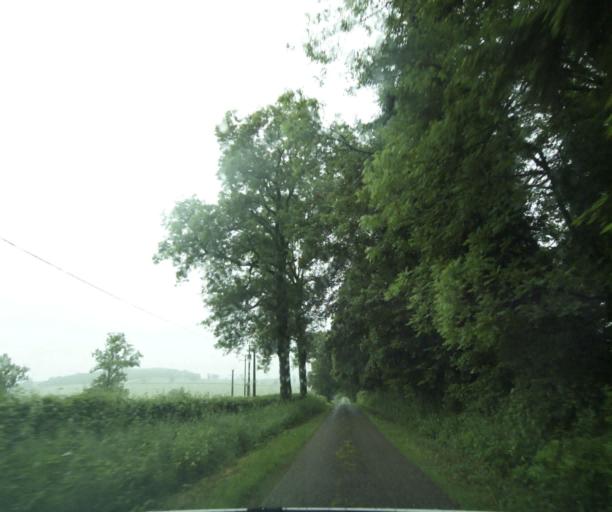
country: FR
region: Bourgogne
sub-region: Departement de Saone-et-Loire
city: Charolles
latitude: 46.4144
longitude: 4.2149
